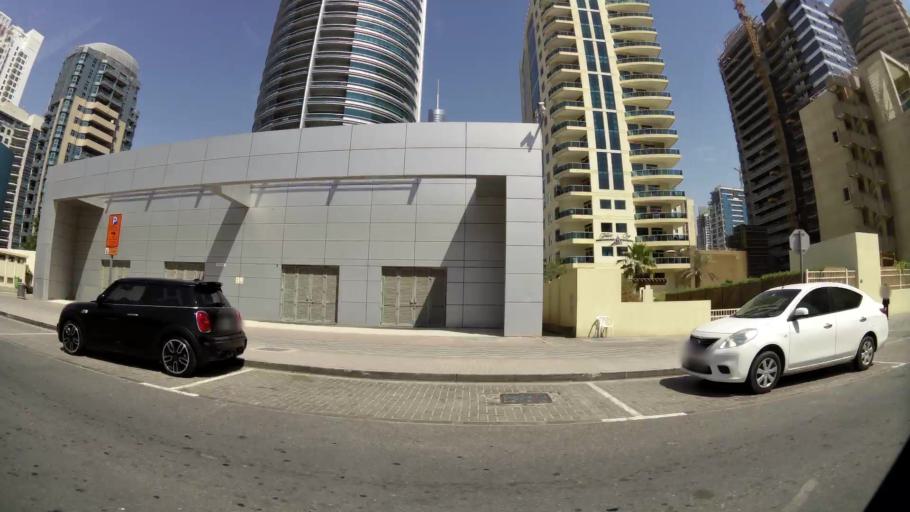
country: AE
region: Dubai
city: Dubai
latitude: 25.0715
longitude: 55.1366
